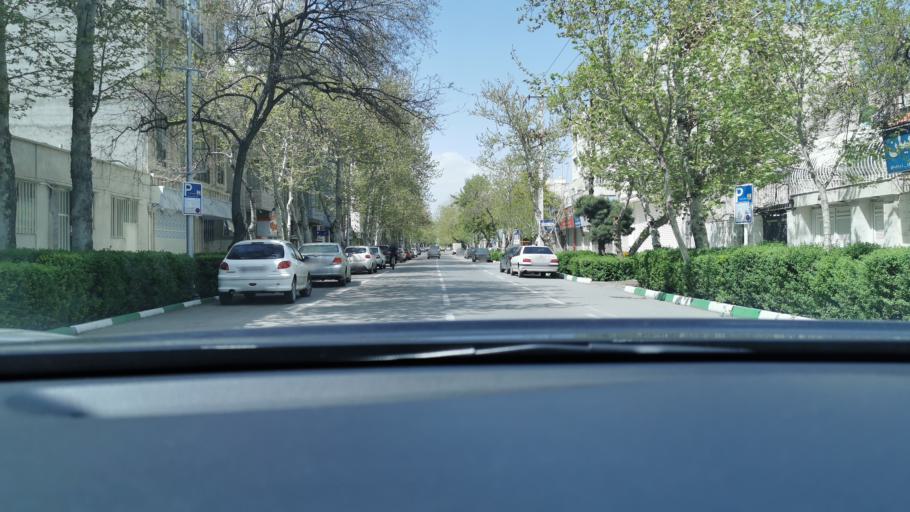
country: IR
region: Razavi Khorasan
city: Mashhad
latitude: 36.2965
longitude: 59.5969
